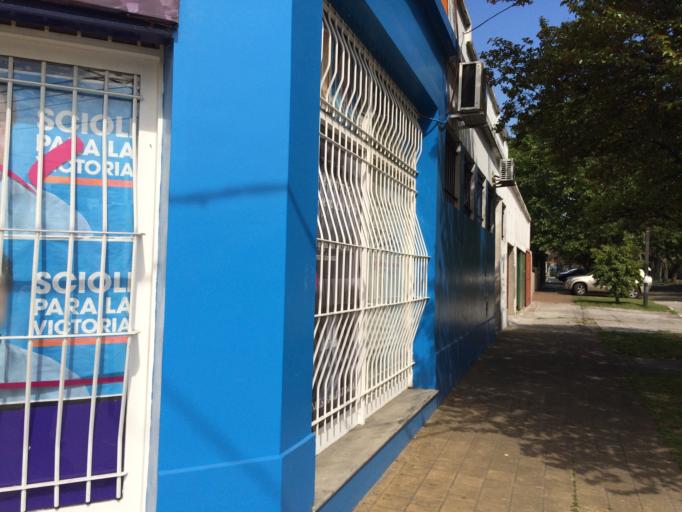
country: AR
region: Buenos Aires
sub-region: Partido de Lomas de Zamora
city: Lomas de Zamora
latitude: -34.7530
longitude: -58.3951
